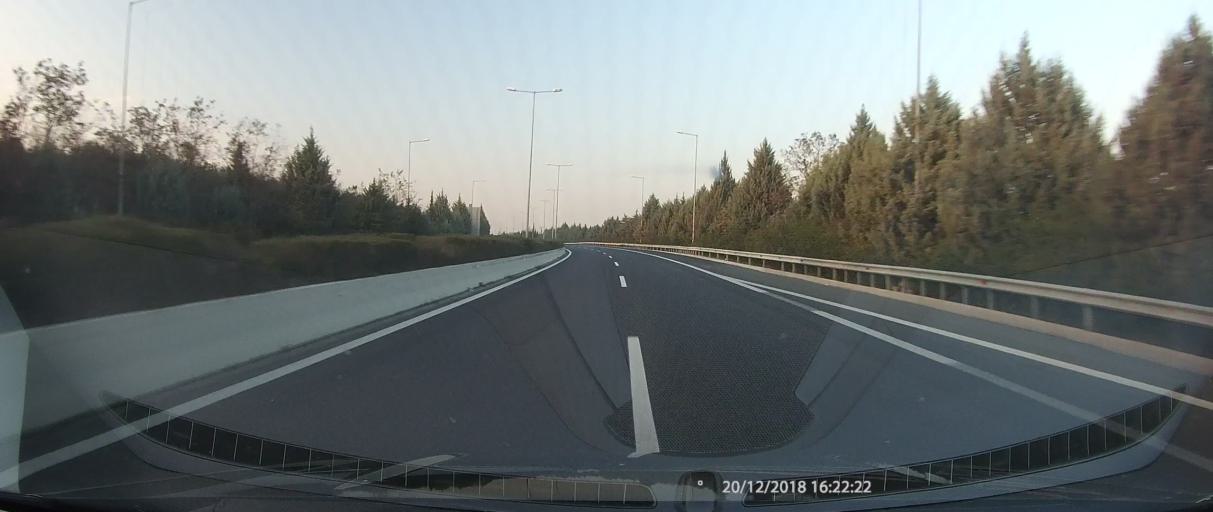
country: GR
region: Thessaly
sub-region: Nomos Magnisias
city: Sourpi
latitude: 39.0685
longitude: 22.8870
